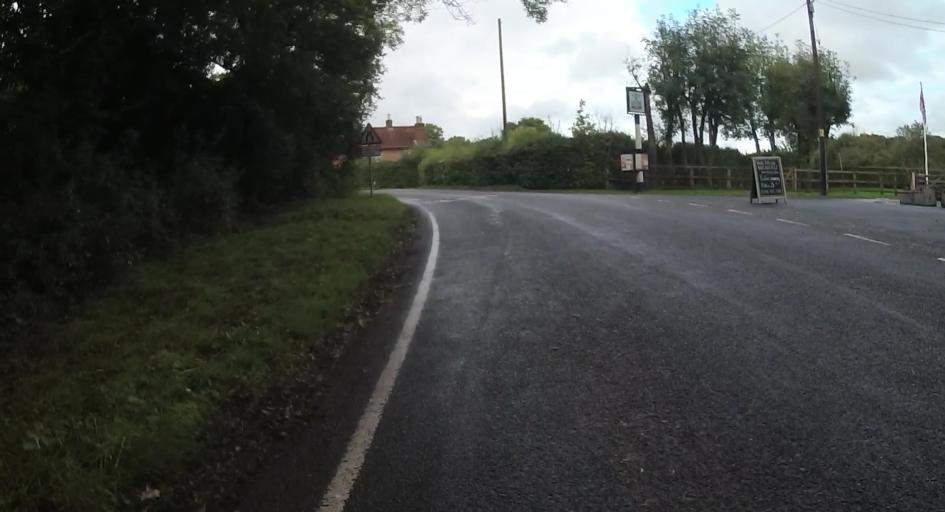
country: GB
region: England
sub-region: Hampshire
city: Tadley
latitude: 51.3402
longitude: -1.1631
